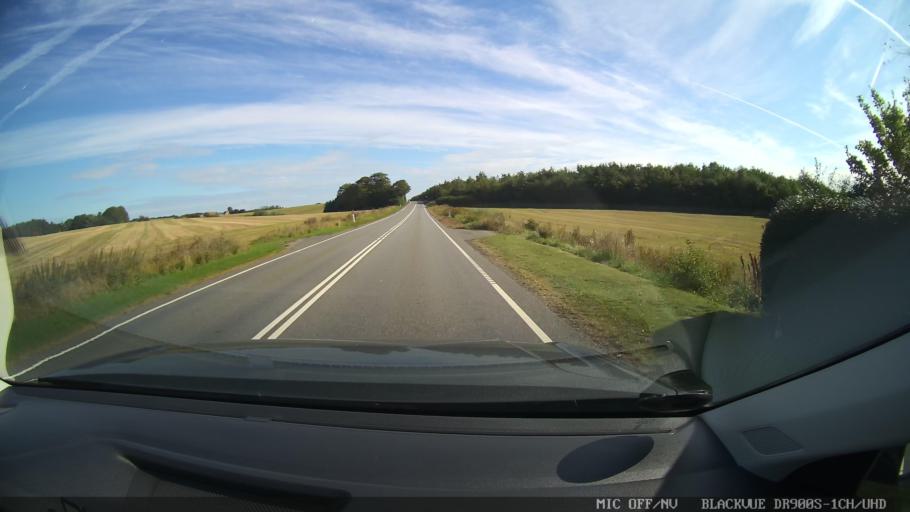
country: DK
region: North Denmark
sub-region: Mariagerfjord Kommune
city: Hadsund
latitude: 56.7772
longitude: 10.0067
